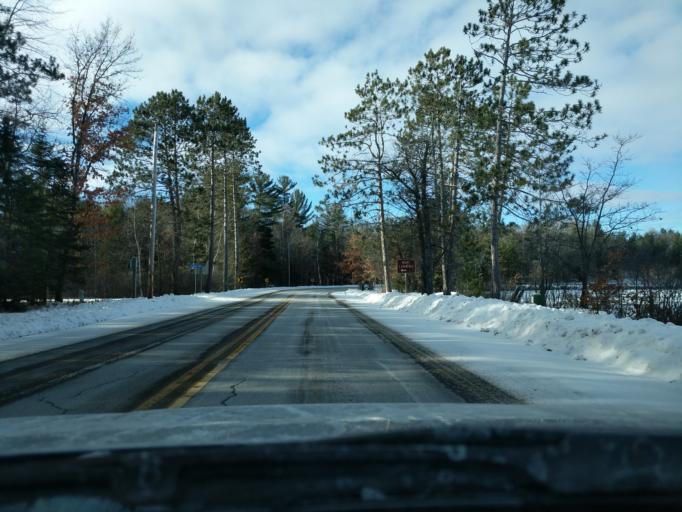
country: US
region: Wisconsin
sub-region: Vilas County
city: Eagle River
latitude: 45.7742
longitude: -89.0741
